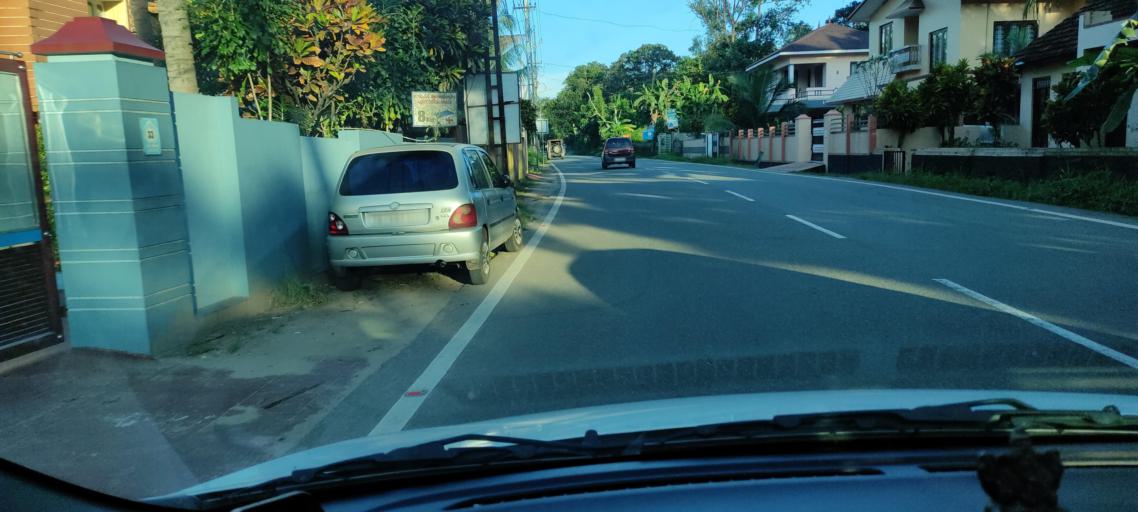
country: IN
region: Kerala
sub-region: Pattanamtitta
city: Adur
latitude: 9.1448
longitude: 76.7703
